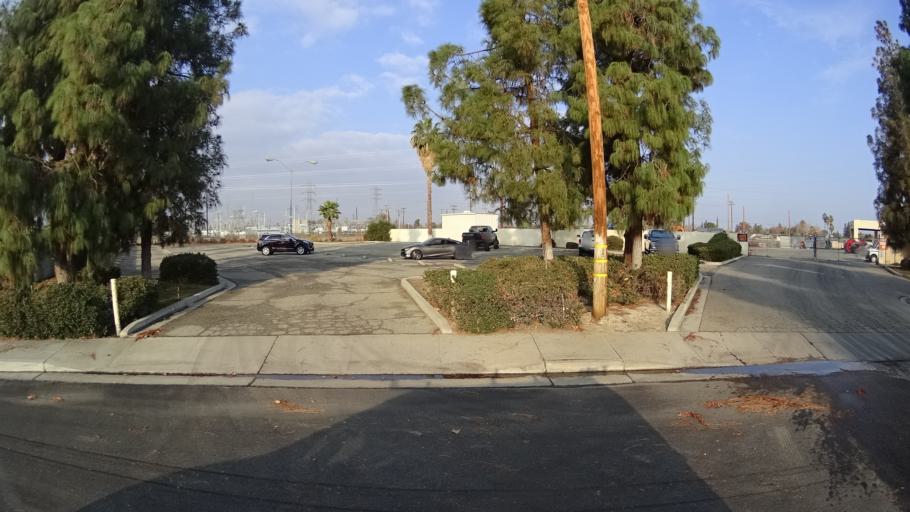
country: US
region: California
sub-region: Kern County
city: Bakersfield
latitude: 35.3166
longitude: -119.0652
